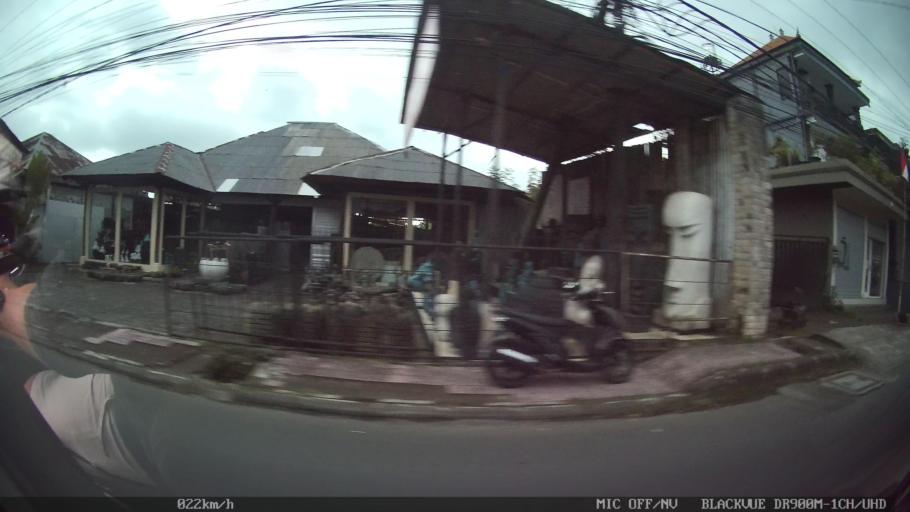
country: ID
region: Bali
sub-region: Kabupaten Gianyar
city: Ubud
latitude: -8.4951
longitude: 115.2735
